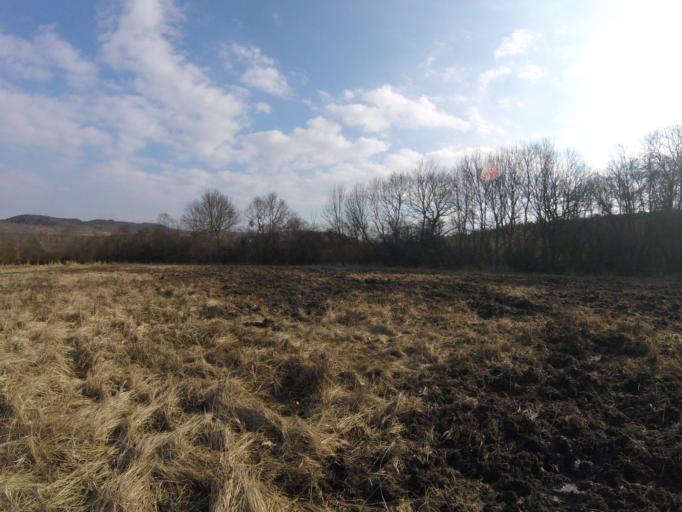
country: HU
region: Heves
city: Egerszalok
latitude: 47.8446
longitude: 20.3259
